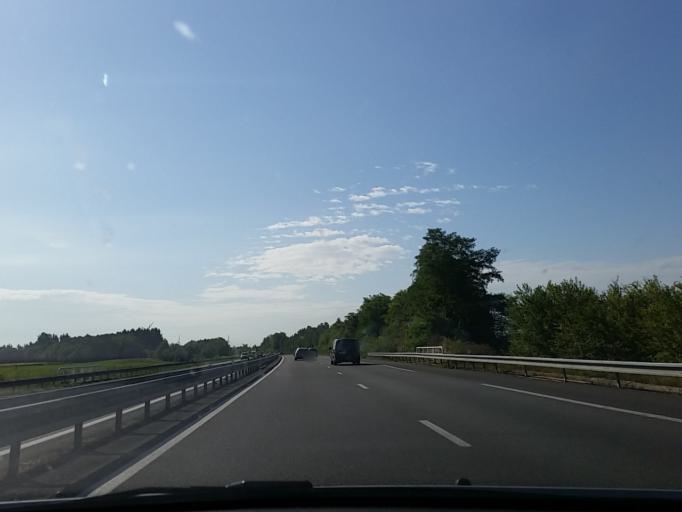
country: FR
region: Centre
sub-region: Departement du Cher
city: Mehun-sur-Yevre
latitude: 47.1201
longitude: 2.1939
